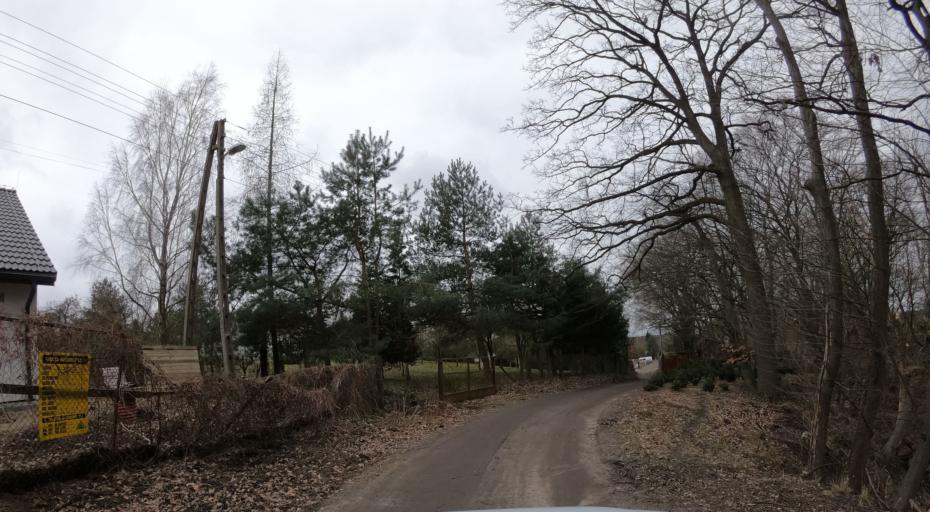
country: PL
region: West Pomeranian Voivodeship
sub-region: Szczecin
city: Szczecin
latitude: 53.4957
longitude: 14.4852
